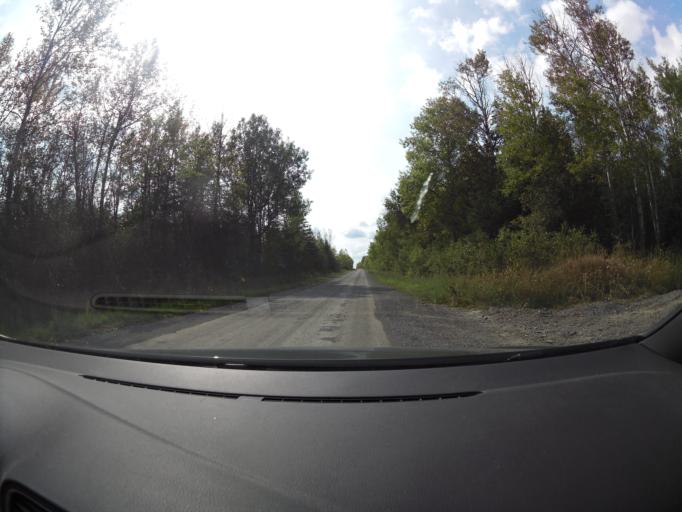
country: CA
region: Ontario
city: Arnprior
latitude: 45.3632
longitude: -76.1752
